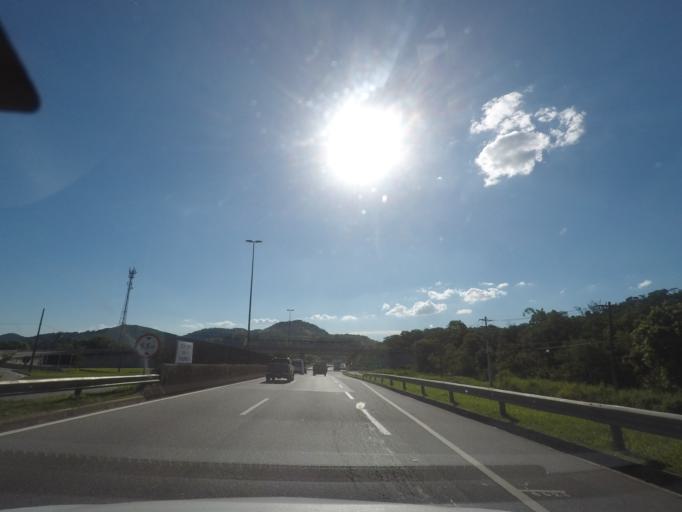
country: BR
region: Rio de Janeiro
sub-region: Petropolis
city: Petropolis
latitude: -22.6561
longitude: -43.1261
